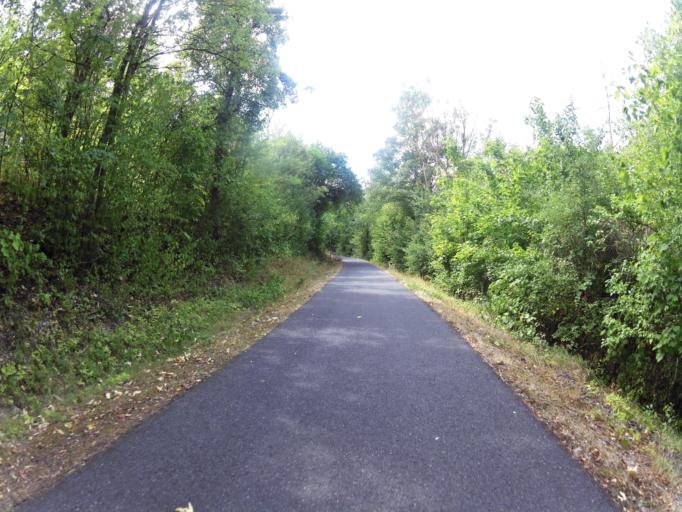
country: DE
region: Bavaria
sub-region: Regierungsbezirk Unterfranken
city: Ochsenfurt
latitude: 49.6675
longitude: 10.0457
